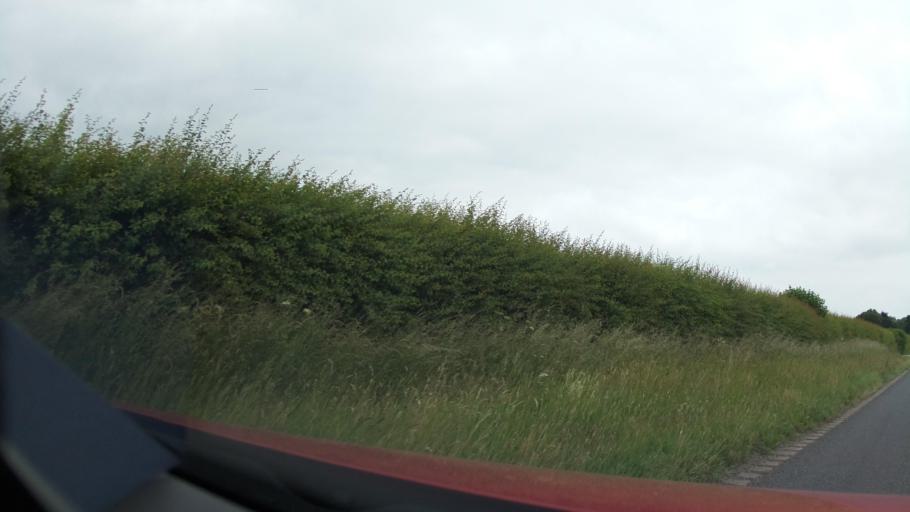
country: GB
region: England
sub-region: District of Rutland
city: Empingham
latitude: 52.6546
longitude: -0.6041
